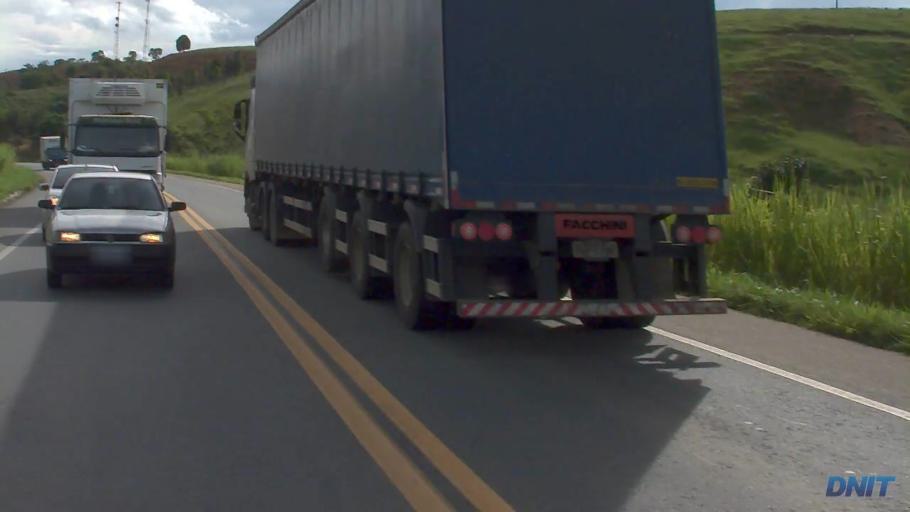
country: BR
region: Minas Gerais
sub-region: Belo Oriente
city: Belo Oriente
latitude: -19.2183
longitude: -42.3081
